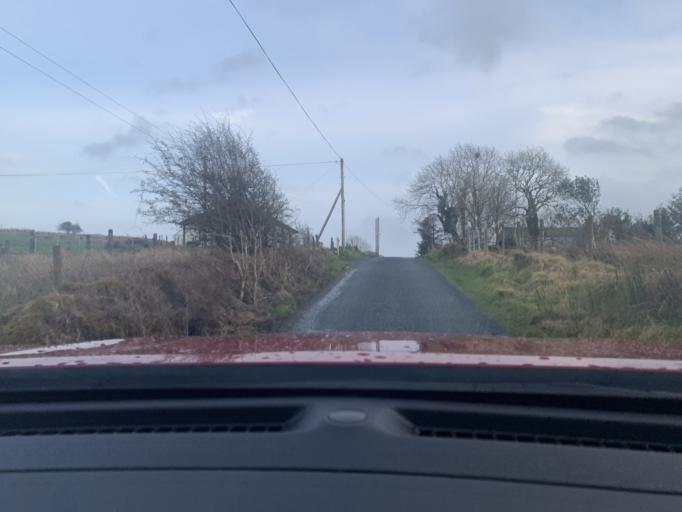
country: IE
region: Connaught
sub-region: Roscommon
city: Ballaghaderreen
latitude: 53.9528
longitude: -8.5235
